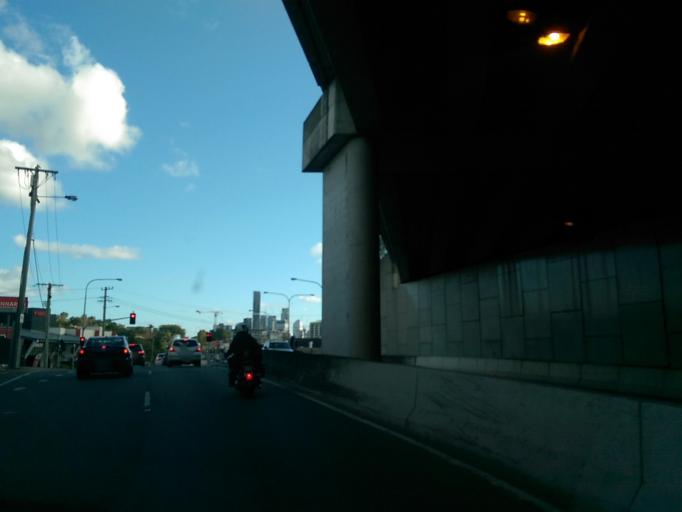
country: AU
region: Queensland
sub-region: Brisbane
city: Windsor
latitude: -27.4415
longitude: 153.0390
